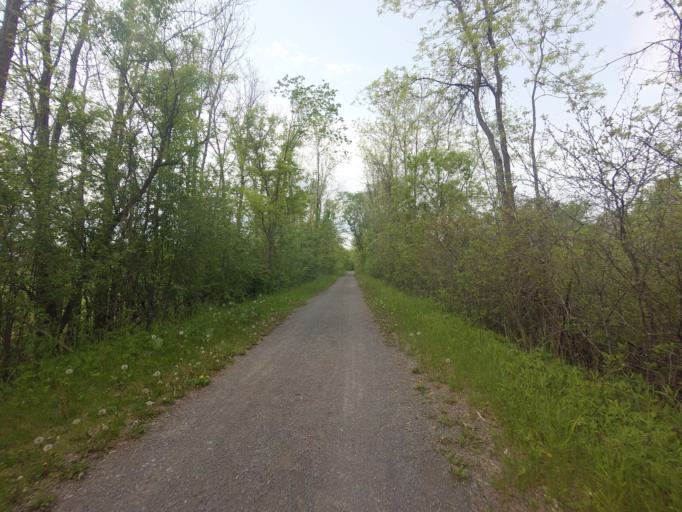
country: CA
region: Ontario
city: Kingston
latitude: 44.2945
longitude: -76.5588
